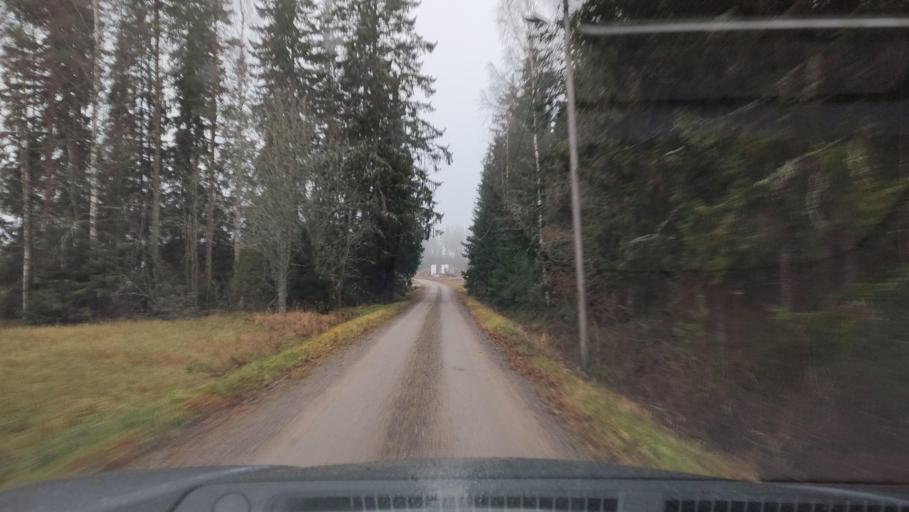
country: FI
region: Southern Ostrobothnia
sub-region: Suupohja
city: Karijoki
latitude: 62.1951
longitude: 21.7819
